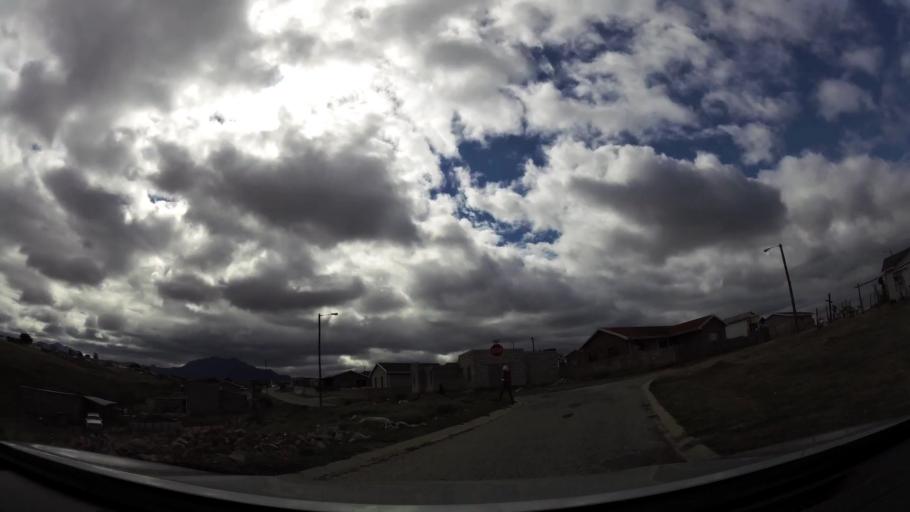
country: ZA
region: Western Cape
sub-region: Eden District Municipality
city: George
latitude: -34.0254
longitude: 22.4749
